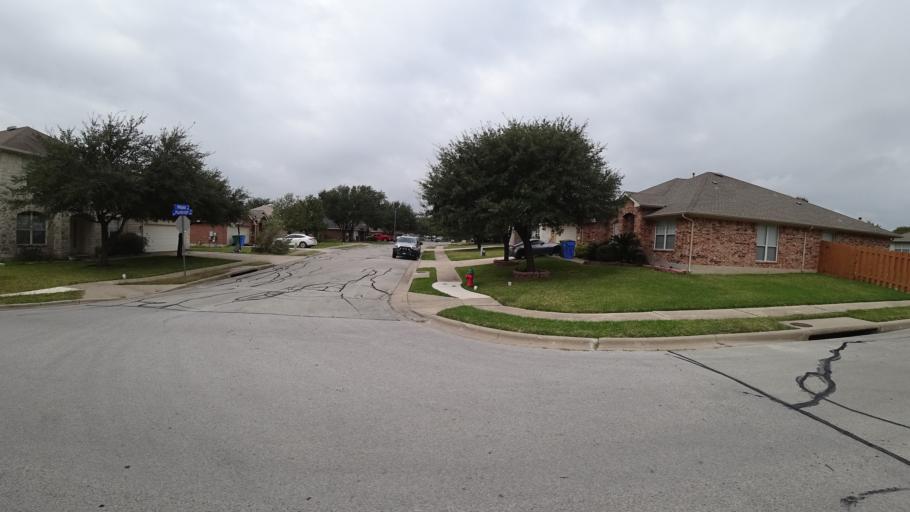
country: US
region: Texas
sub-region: Travis County
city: Pflugerville
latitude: 30.4349
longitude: -97.6045
